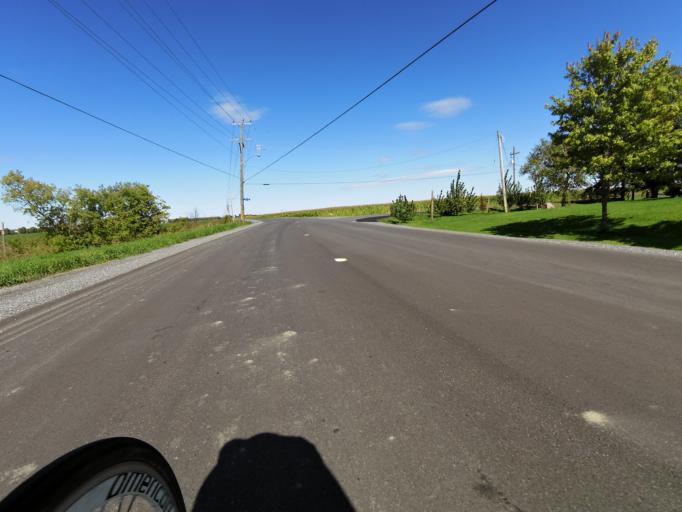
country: CA
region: Ontario
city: Bells Corners
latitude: 45.2281
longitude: -75.8622
